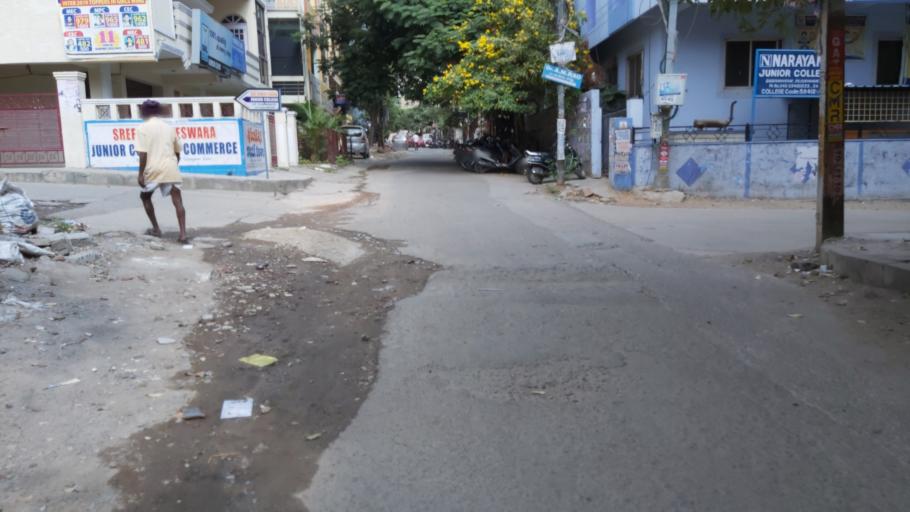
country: IN
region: Telangana
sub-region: Rangareddi
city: Gaddi Annaram
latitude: 17.3675
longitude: 78.5212
